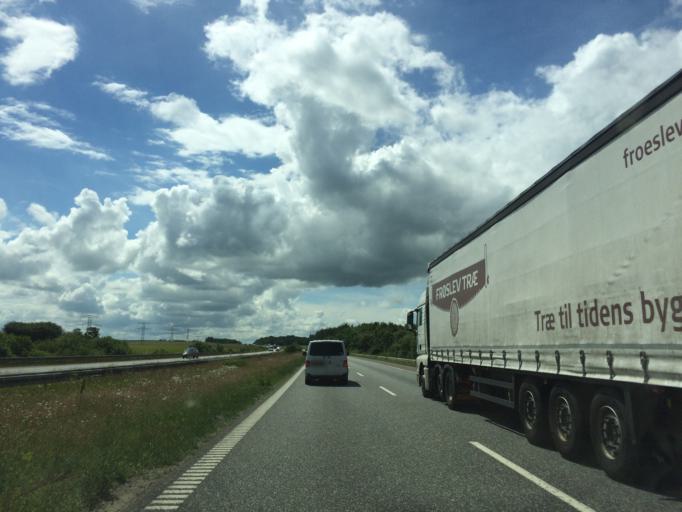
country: DK
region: North Denmark
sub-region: Rebild Kommune
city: Stovring
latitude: 56.8637
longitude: 9.7788
